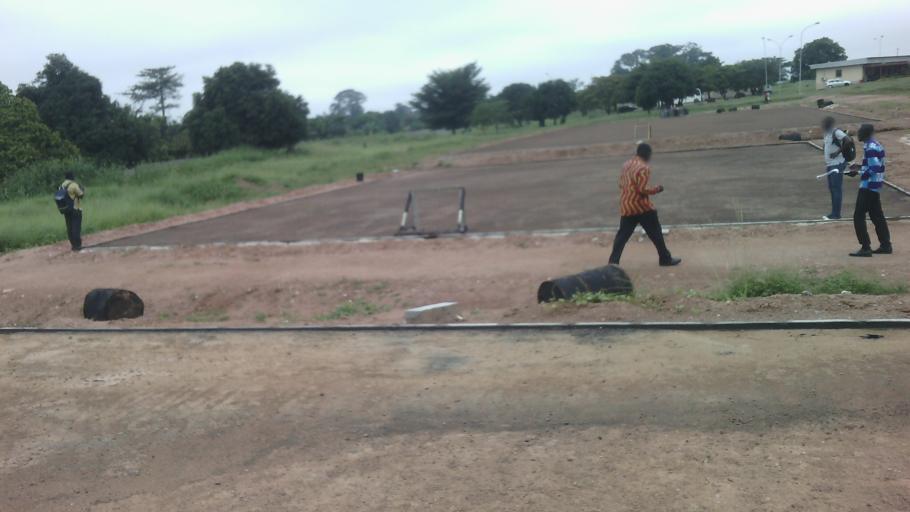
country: CI
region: Vallee du Bandama
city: Bouake
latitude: 7.6865
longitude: -5.0684
